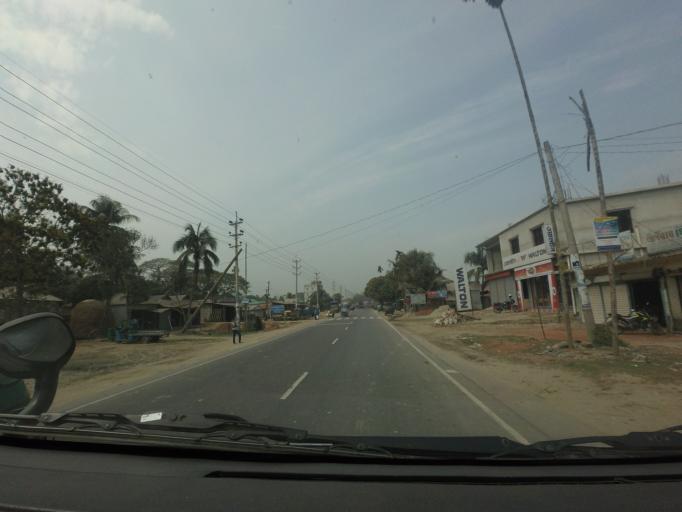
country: BD
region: Dhaka
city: Bajitpur
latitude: 24.2083
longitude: 90.8571
